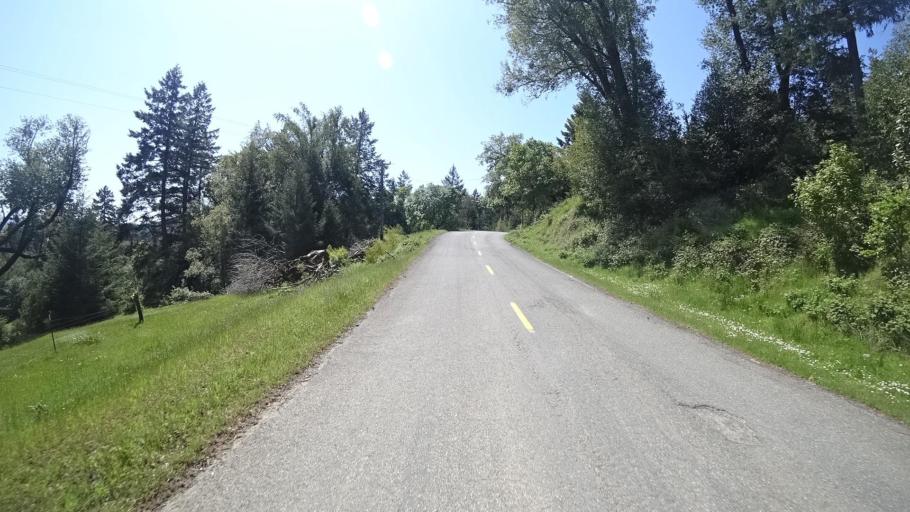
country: US
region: California
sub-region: Humboldt County
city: Redway
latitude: 40.1513
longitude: -123.6247
